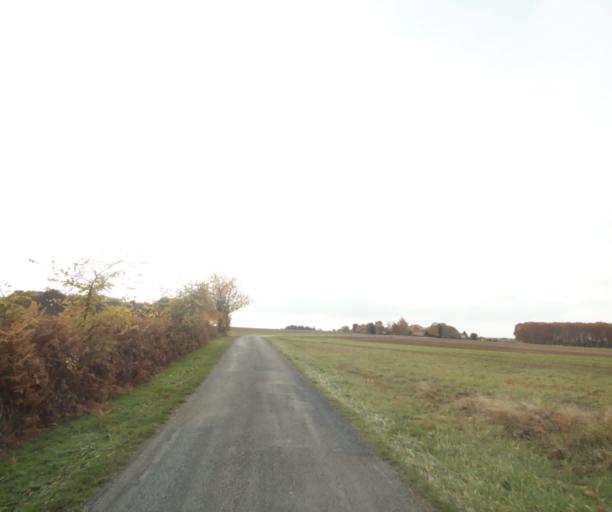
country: FR
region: Poitou-Charentes
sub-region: Departement de la Charente-Maritime
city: Saint-Georges-des-Coteaux
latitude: 45.7864
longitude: -0.7243
